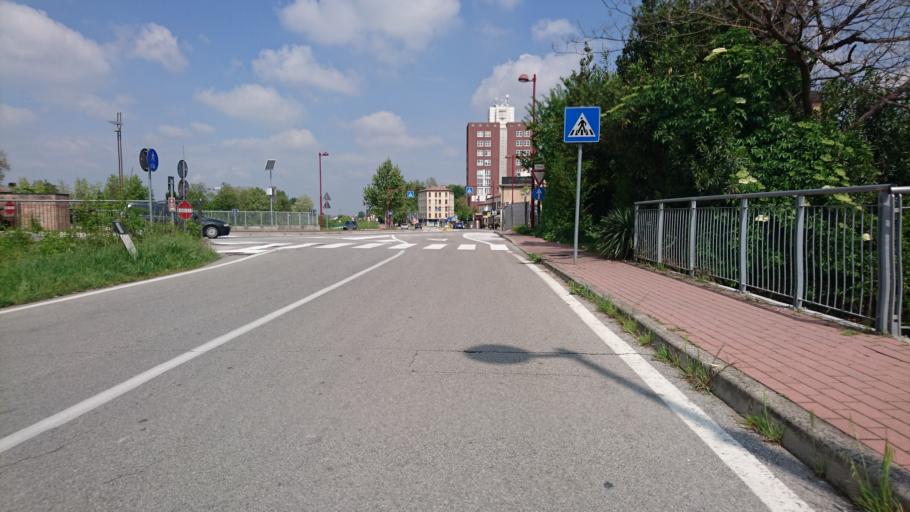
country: IT
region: Veneto
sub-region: Provincia di Padova
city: Mejaniga
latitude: 45.4485
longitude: 11.8964
